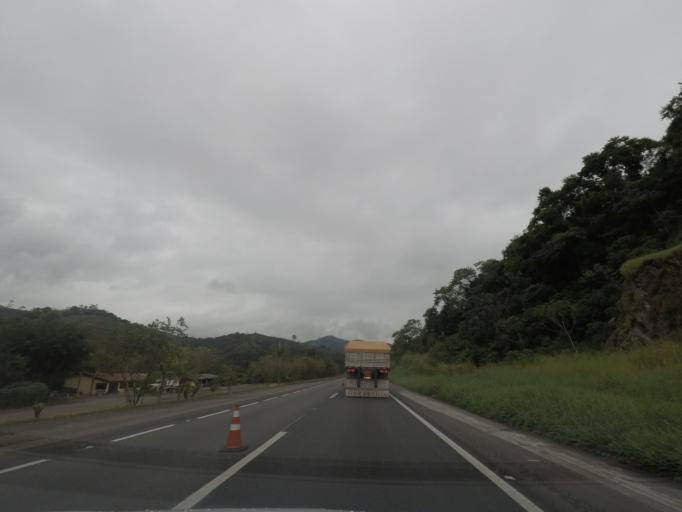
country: BR
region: Sao Paulo
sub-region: Cajati
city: Cajati
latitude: -24.8115
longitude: -48.2105
